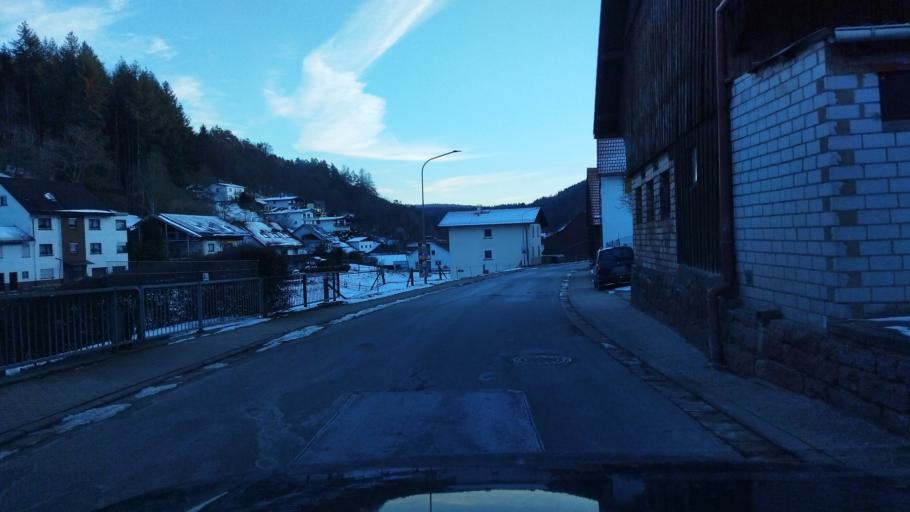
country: DE
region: Baden-Wuerttemberg
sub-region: Karlsruhe Region
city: Eberbach
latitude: 49.5137
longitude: 9.0106
